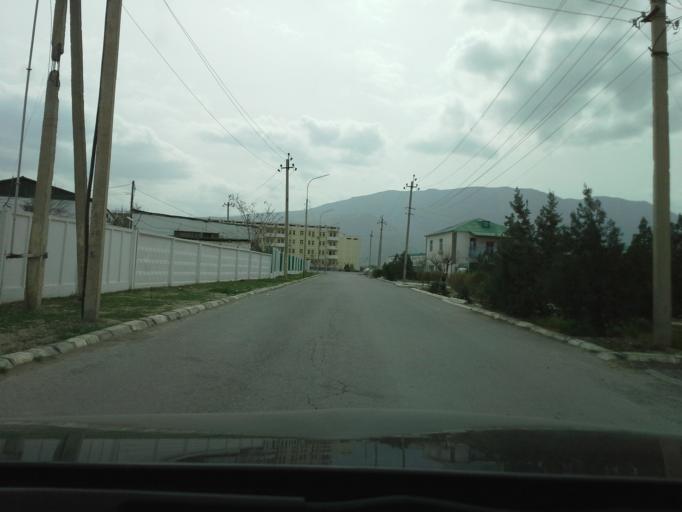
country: TM
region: Ahal
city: Abadan
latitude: 38.0585
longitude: 58.1416
